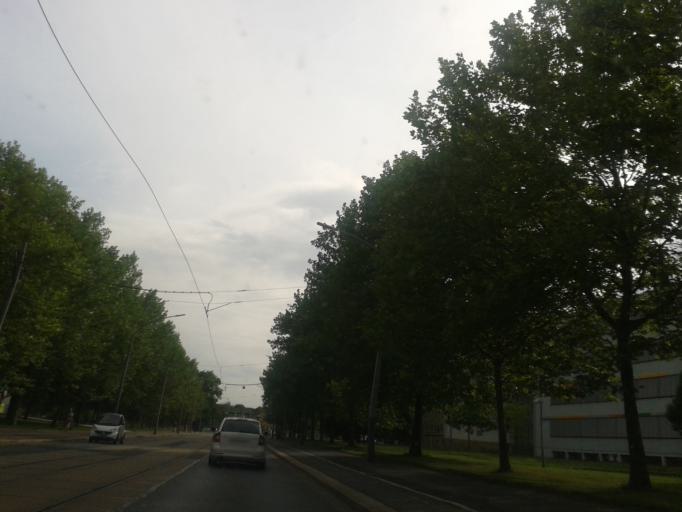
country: DE
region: Saxony
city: Dresden
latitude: 51.0489
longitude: 13.7566
